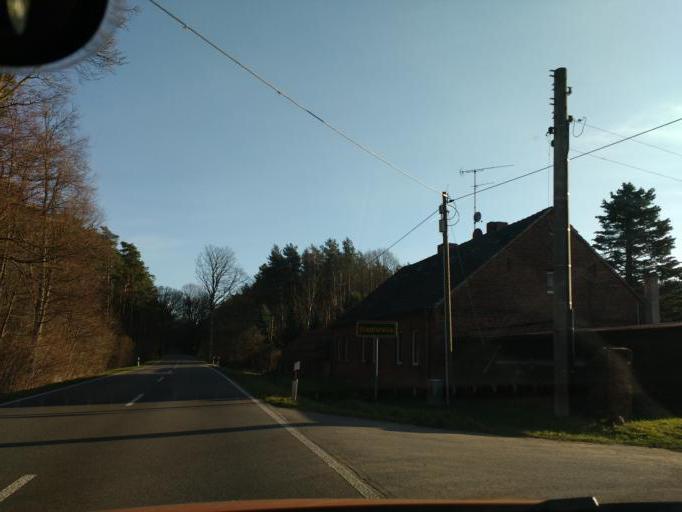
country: DE
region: Brandenburg
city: Protzel
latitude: 52.6476
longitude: 13.9158
